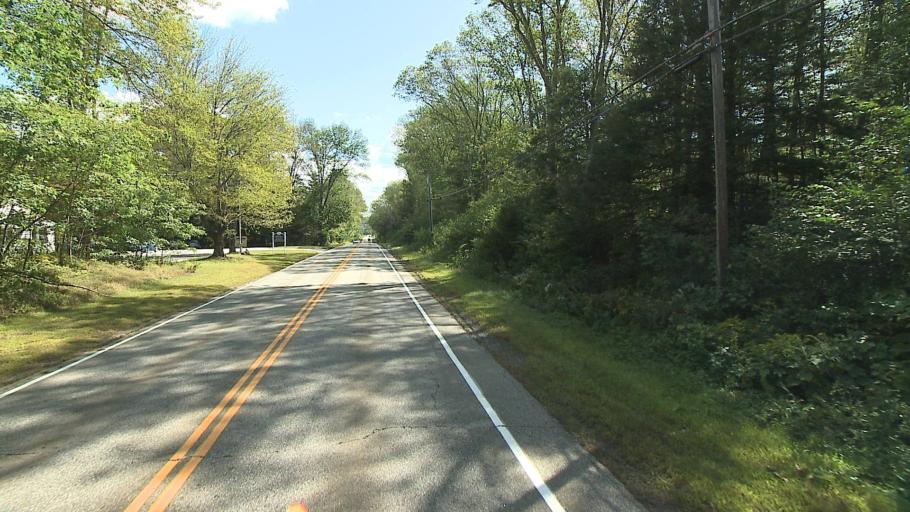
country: US
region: Connecticut
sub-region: Windham County
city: South Woodstock
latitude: 41.8614
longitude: -71.9778
